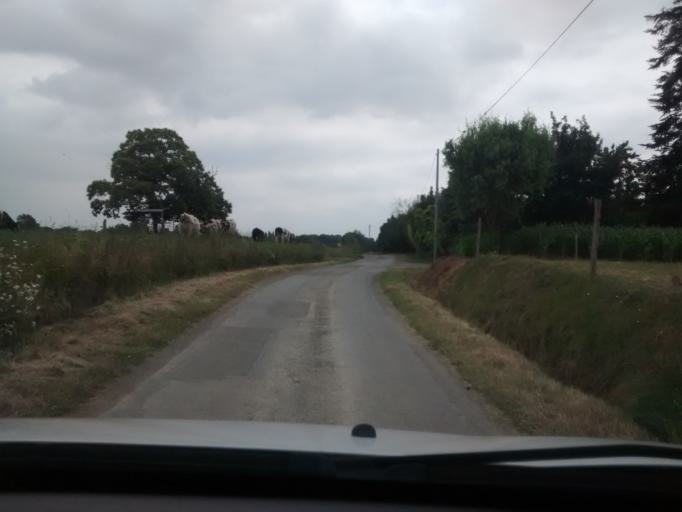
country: FR
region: Brittany
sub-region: Departement d'Ille-et-Vilaine
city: Noyal-sur-Vilaine
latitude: 48.1255
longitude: -1.5031
